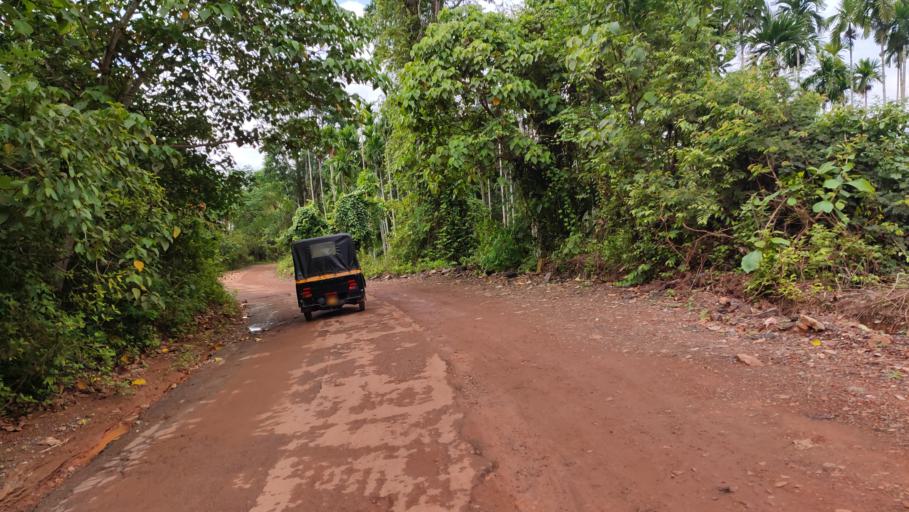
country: IN
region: Kerala
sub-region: Kasaragod District
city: Kasaragod
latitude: 12.5262
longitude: 75.0711
